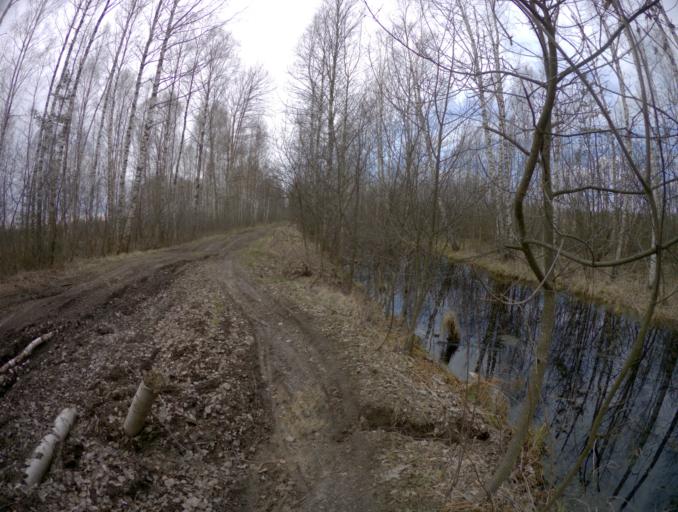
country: RU
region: Vladimir
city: Raduzhnyy
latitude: 55.9095
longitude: 40.2296
